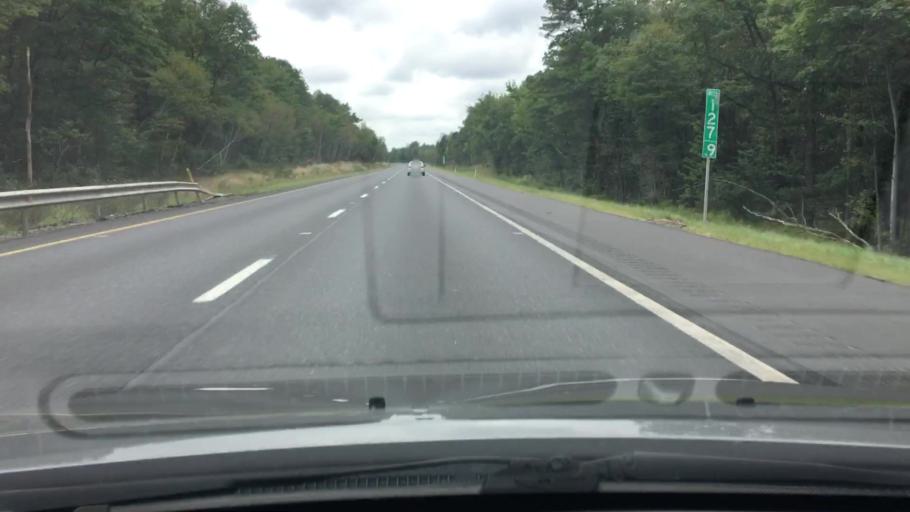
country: US
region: Pennsylvania
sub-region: Schuylkill County
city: Mahanoy City
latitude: 40.7876
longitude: -76.1537
